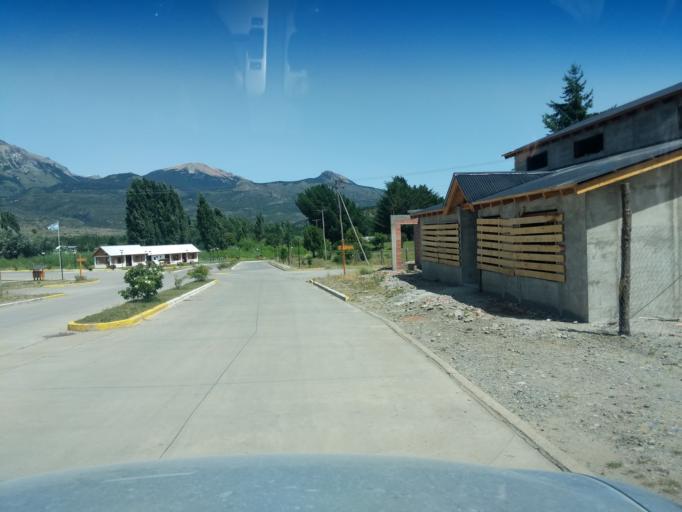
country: CL
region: Los Lagos
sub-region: Provincia de Palena
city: Palena
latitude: -43.5357
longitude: -71.4680
